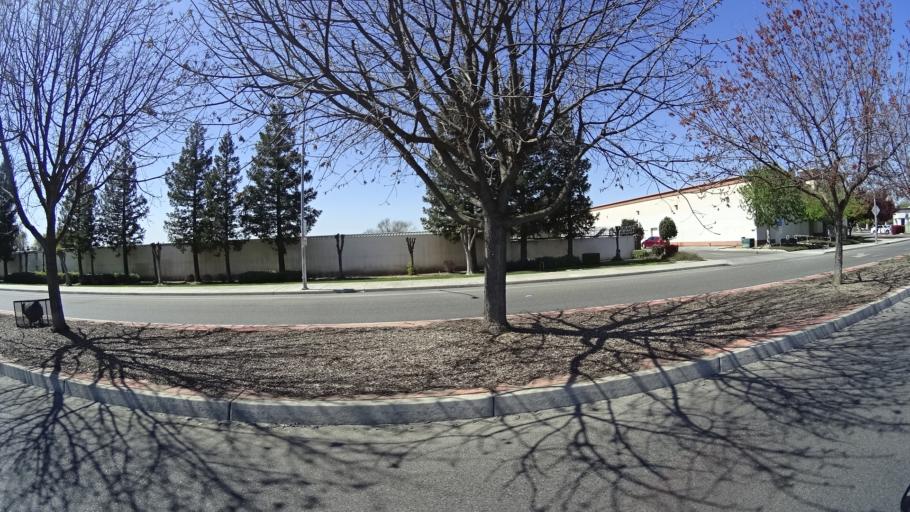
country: US
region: California
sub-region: Fresno County
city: West Park
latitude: 36.7925
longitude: -119.8713
